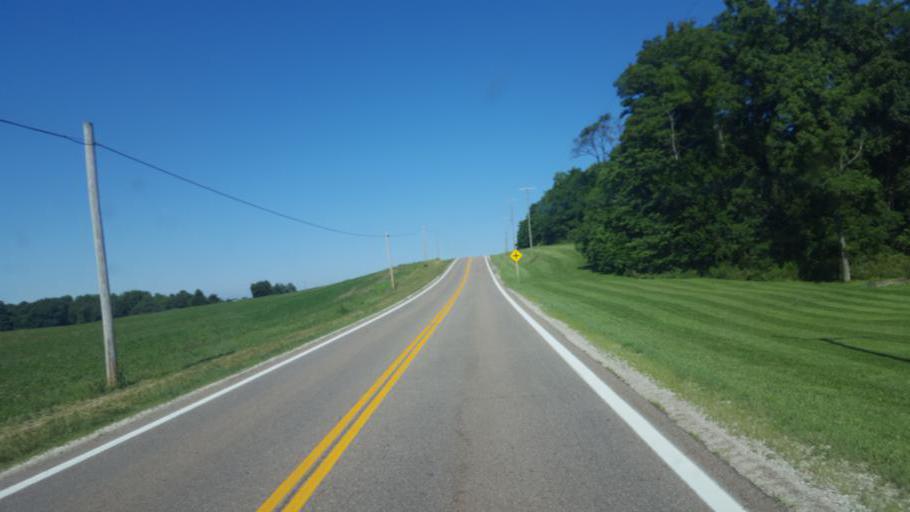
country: US
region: Ohio
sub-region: Knox County
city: Centerburg
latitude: 40.3996
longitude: -82.7278
